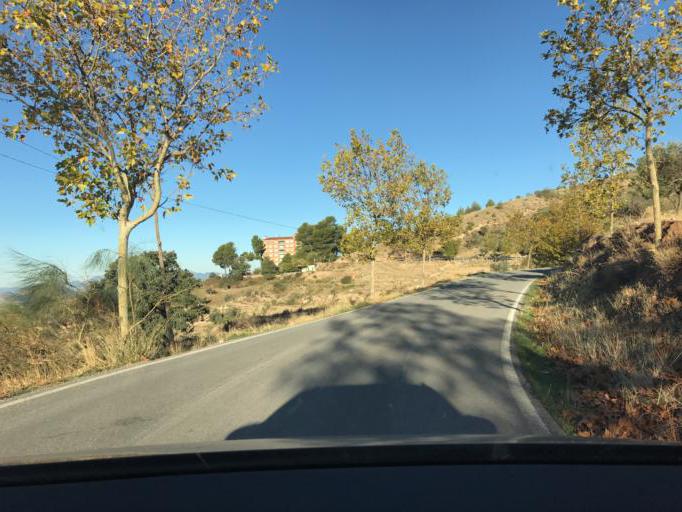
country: ES
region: Andalusia
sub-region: Provincia de Granada
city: Viznar
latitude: 37.2412
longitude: -3.5499
